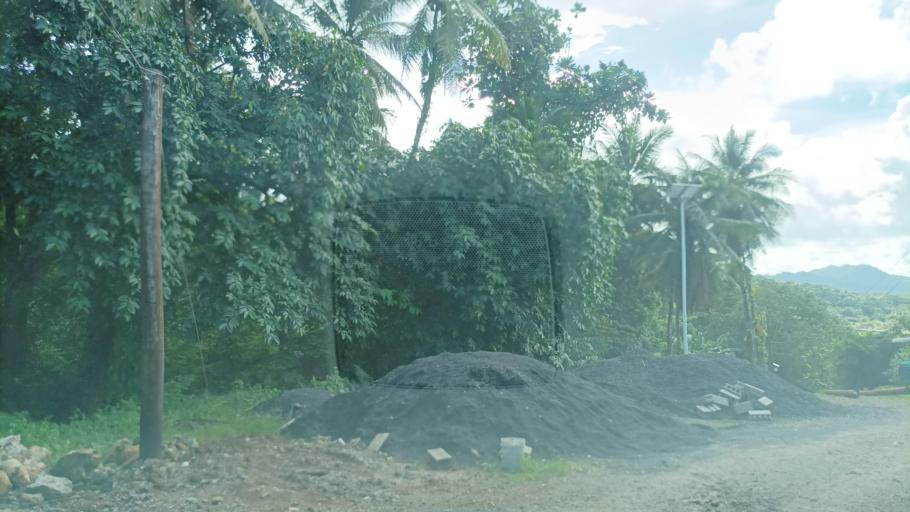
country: FM
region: Pohnpei
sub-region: Kolonia Municipality
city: Kolonia
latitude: 6.9610
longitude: 158.2068
